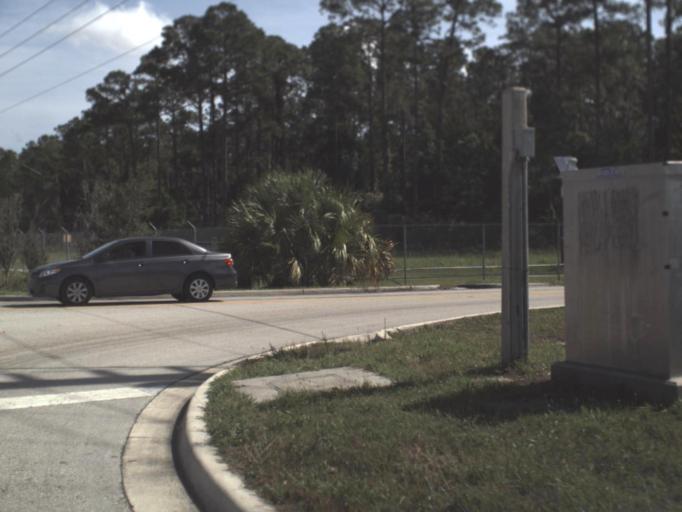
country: US
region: Florida
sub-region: Clay County
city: Orange Park
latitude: 30.1959
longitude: -81.7073
